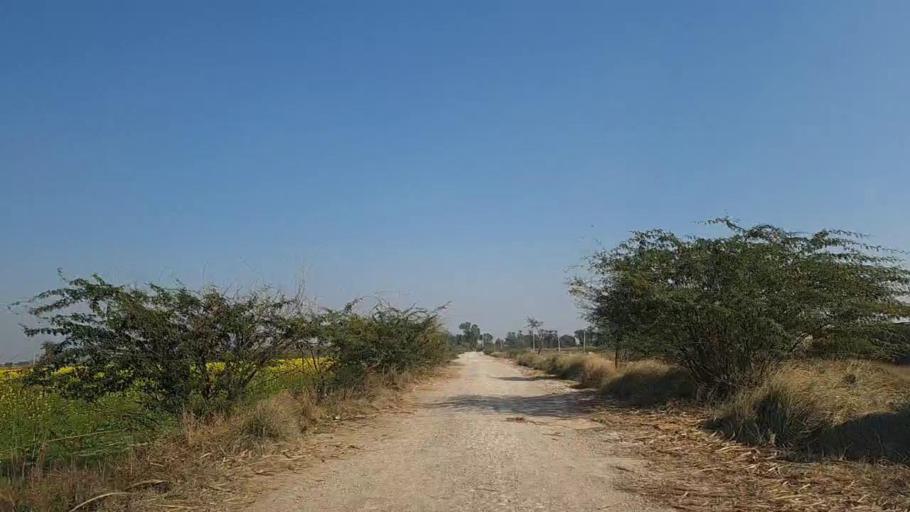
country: PK
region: Sindh
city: Bandhi
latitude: 26.5707
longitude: 68.3059
